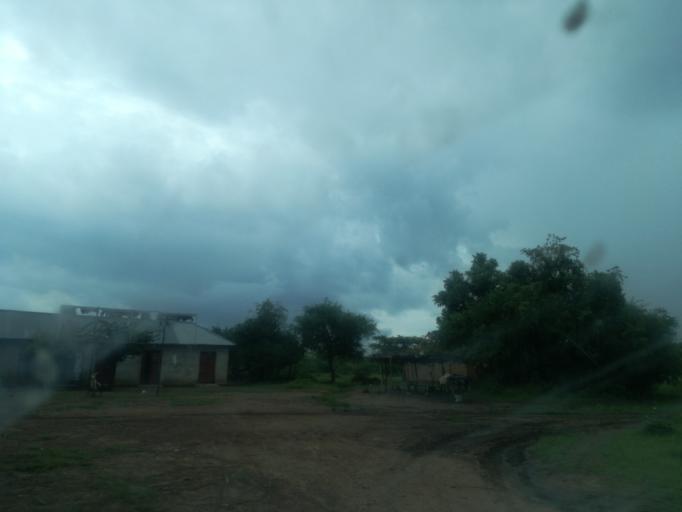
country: TZ
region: Mara
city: Mugumu
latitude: -1.8315
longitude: 34.5709
